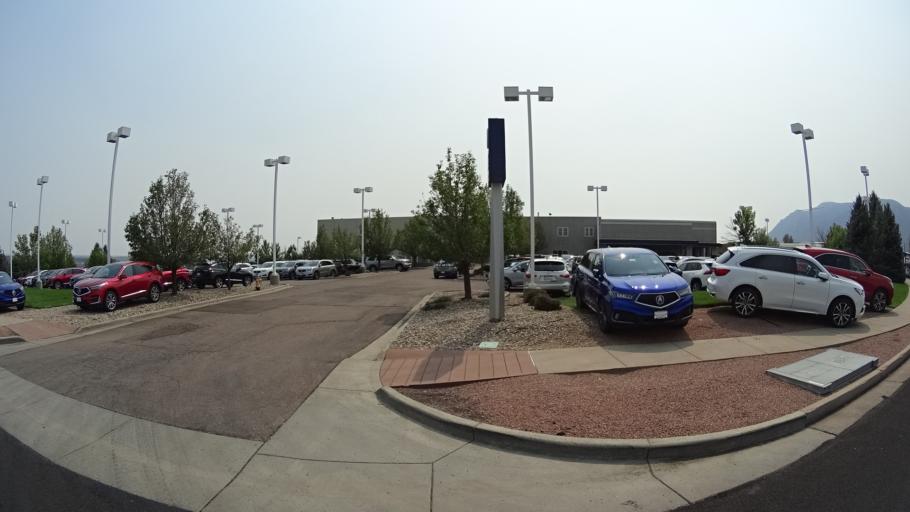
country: US
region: Colorado
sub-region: El Paso County
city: Colorado Springs
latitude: 38.8172
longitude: -104.8401
